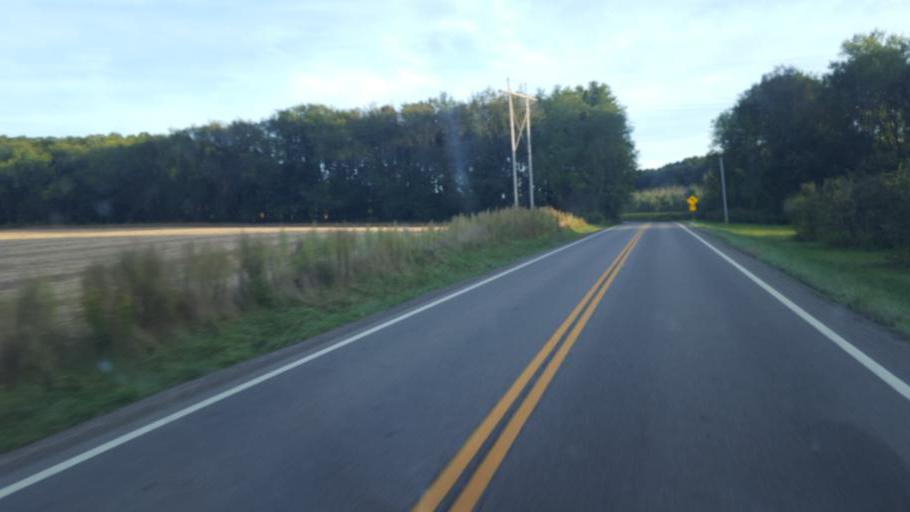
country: US
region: Ohio
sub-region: Ashland County
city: Ashland
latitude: 40.7942
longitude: -82.3838
